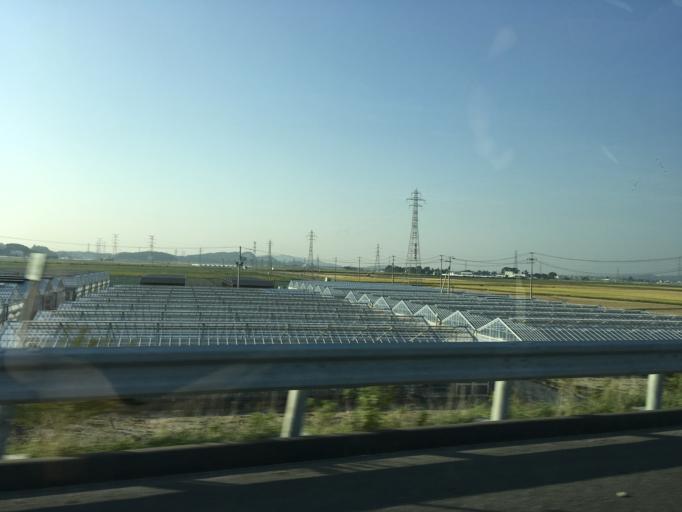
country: JP
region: Miyagi
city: Ishinomaki
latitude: 38.4560
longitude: 141.2746
